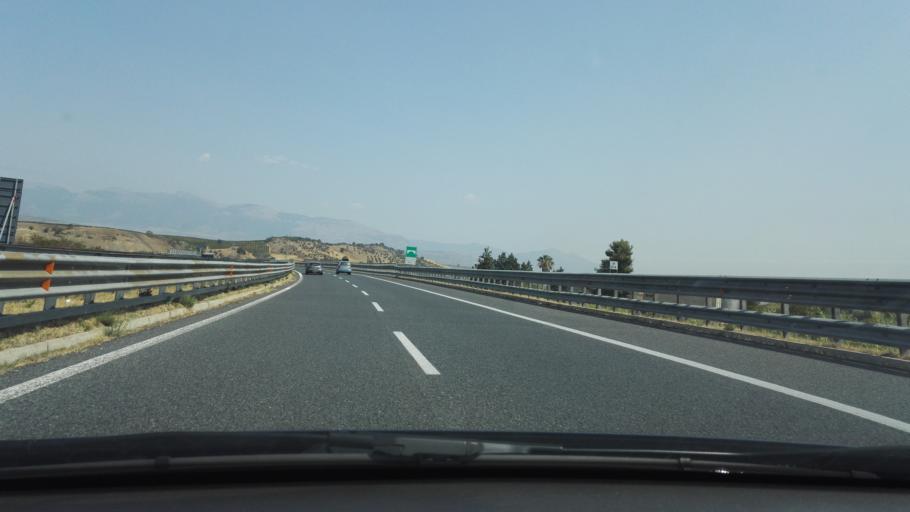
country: IT
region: Calabria
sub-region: Provincia di Cosenza
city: Tarsia
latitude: 39.6332
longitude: 16.2317
